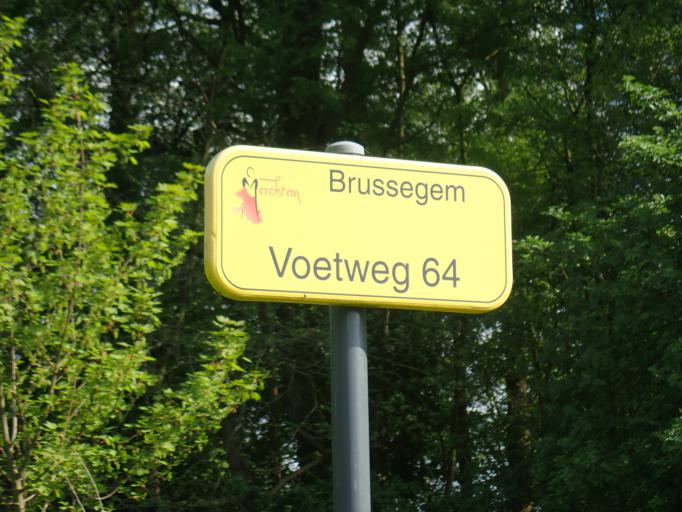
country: BE
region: Flanders
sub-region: Provincie Vlaams-Brabant
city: Wemmel
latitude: 50.9279
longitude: 4.2862
